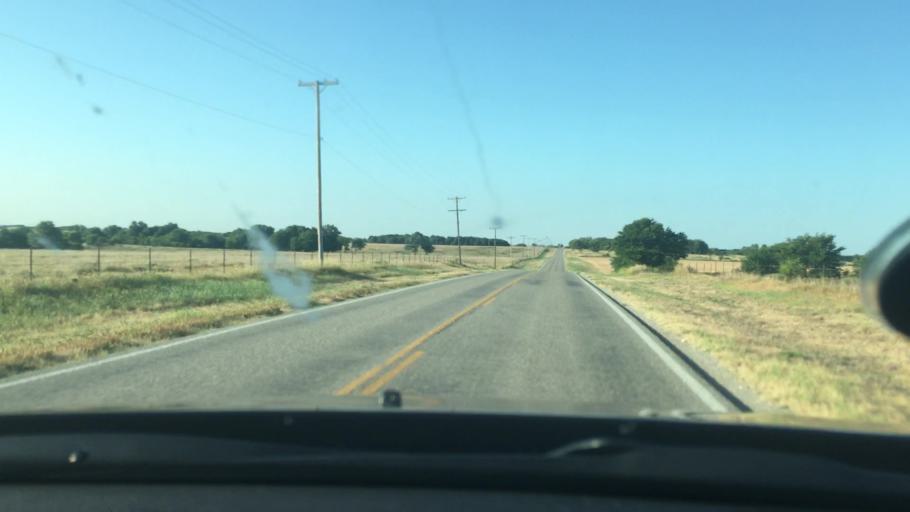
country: US
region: Oklahoma
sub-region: Murray County
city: Sulphur
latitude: 34.5802
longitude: -96.8448
